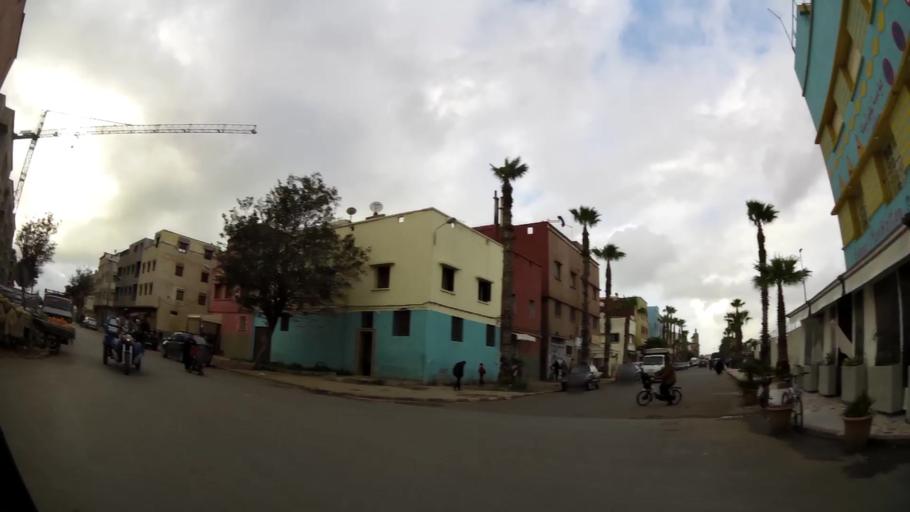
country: MA
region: Grand Casablanca
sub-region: Mohammedia
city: Mohammedia
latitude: 33.6838
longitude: -7.3931
